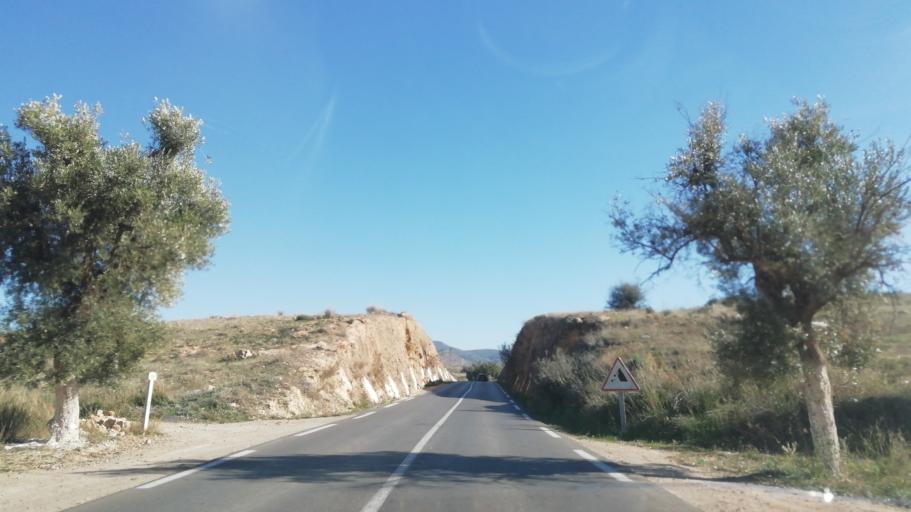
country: DZ
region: Tlemcen
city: Beni Mester
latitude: 34.8397
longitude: -1.4857
